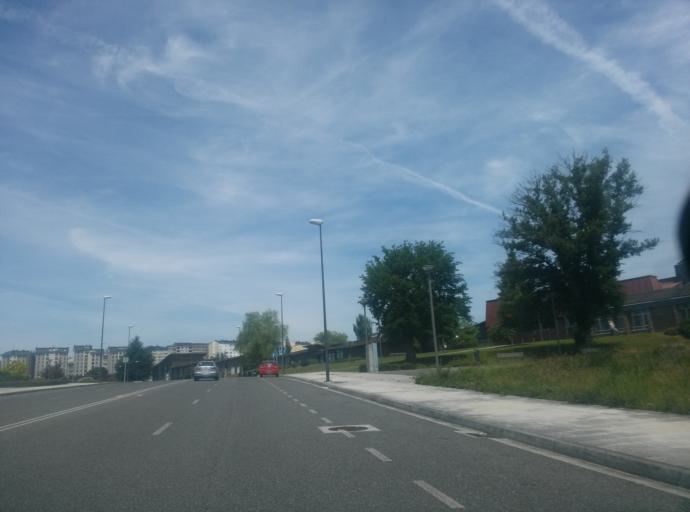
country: ES
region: Galicia
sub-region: Provincia de Lugo
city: Lugo
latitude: 42.9971
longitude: -7.5415
